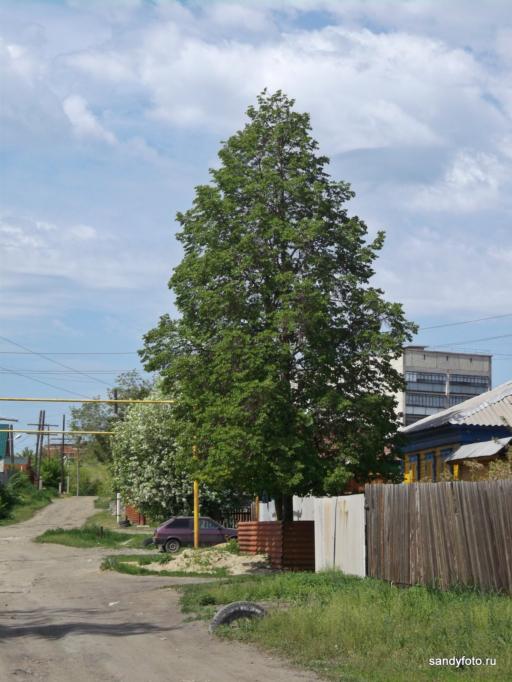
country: RU
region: Chelyabinsk
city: Troitsk
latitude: 54.1022
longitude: 61.5608
